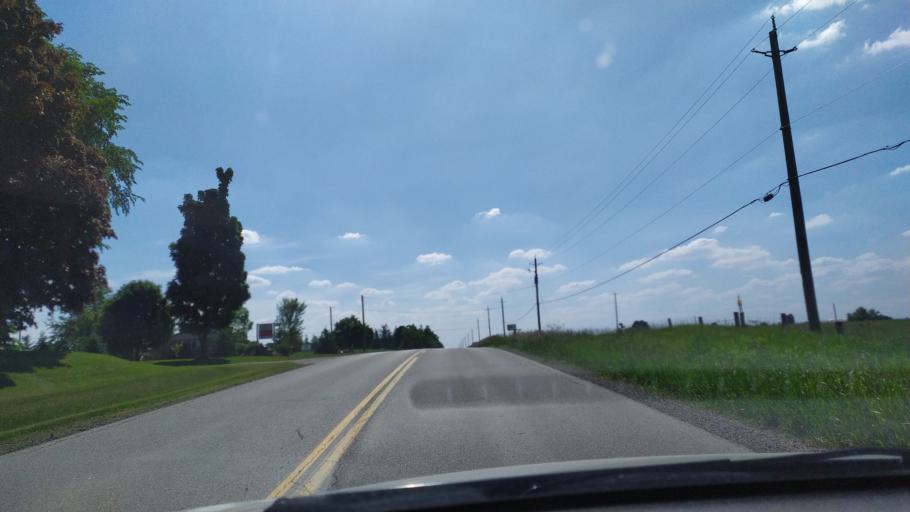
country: CA
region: Ontario
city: Kitchener
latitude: 43.3645
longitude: -80.6031
